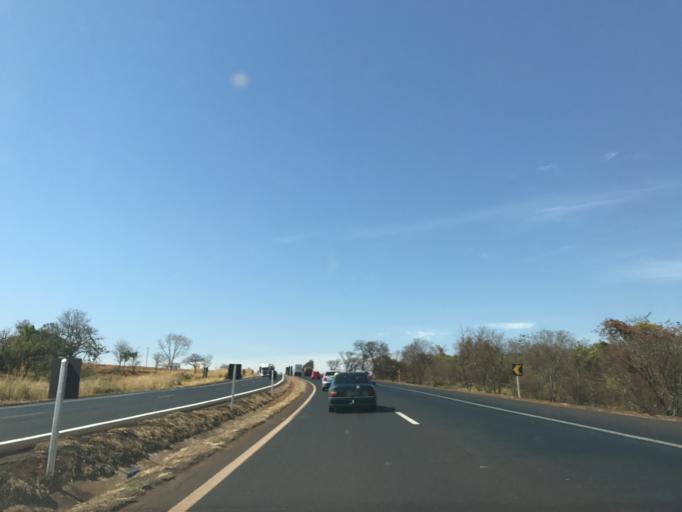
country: BR
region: Minas Gerais
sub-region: Centralina
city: Centralina
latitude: -18.6299
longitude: -49.1845
